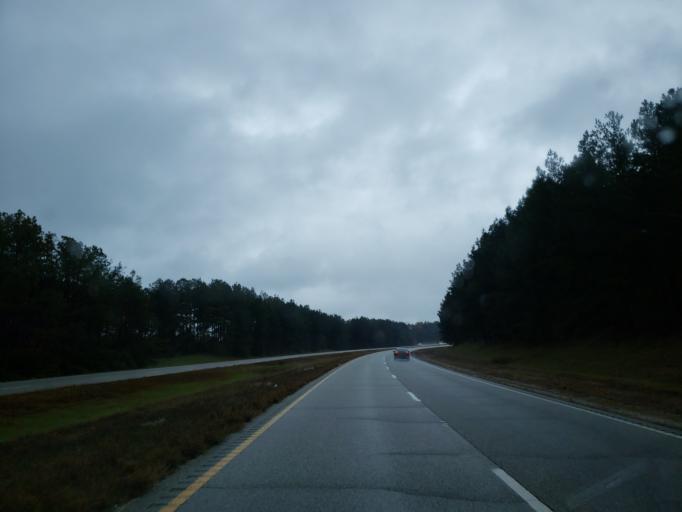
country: US
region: Mississippi
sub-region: Lauderdale County
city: Meridian
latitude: 32.2849
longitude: -88.6983
